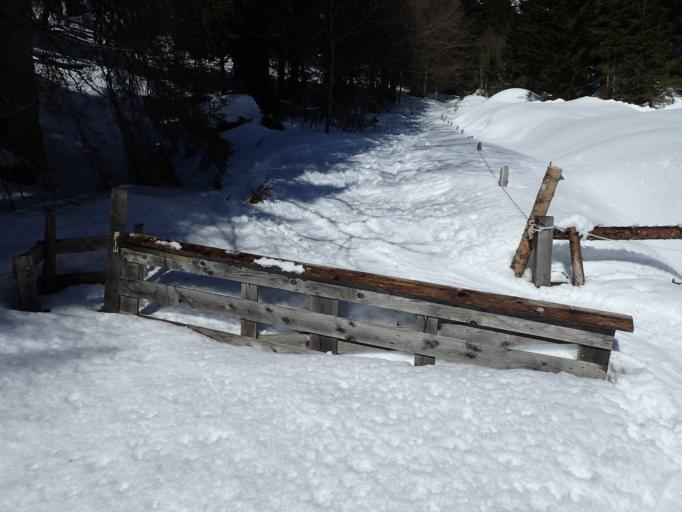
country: AT
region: Salzburg
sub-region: Politischer Bezirk Sankt Johann im Pongau
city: Muhlbach am Hochkonig
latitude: 47.3971
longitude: 13.0797
